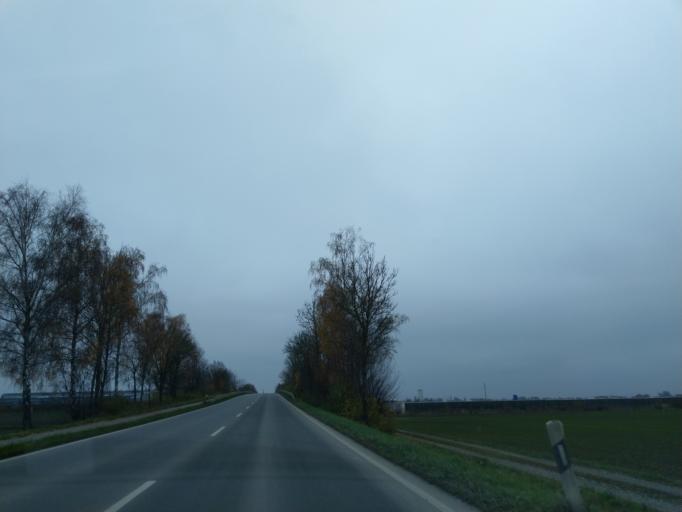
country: DE
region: Bavaria
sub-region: Lower Bavaria
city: Plattling
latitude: 48.8015
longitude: 12.8496
